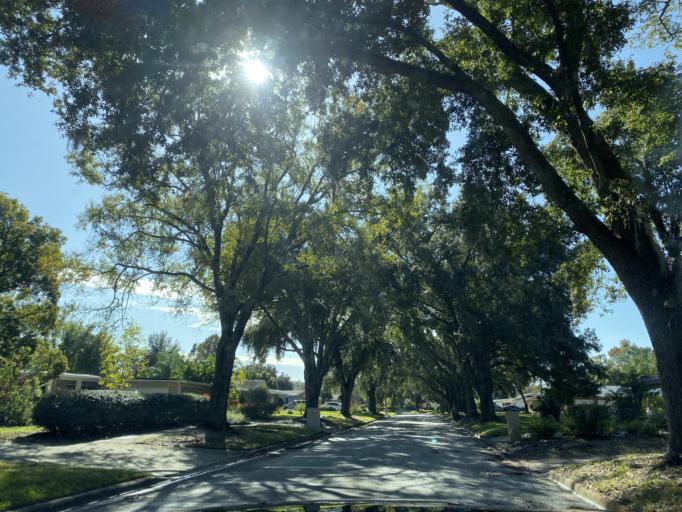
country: US
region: Florida
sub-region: Orange County
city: Azalea Park
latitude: 28.5301
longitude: -81.2634
